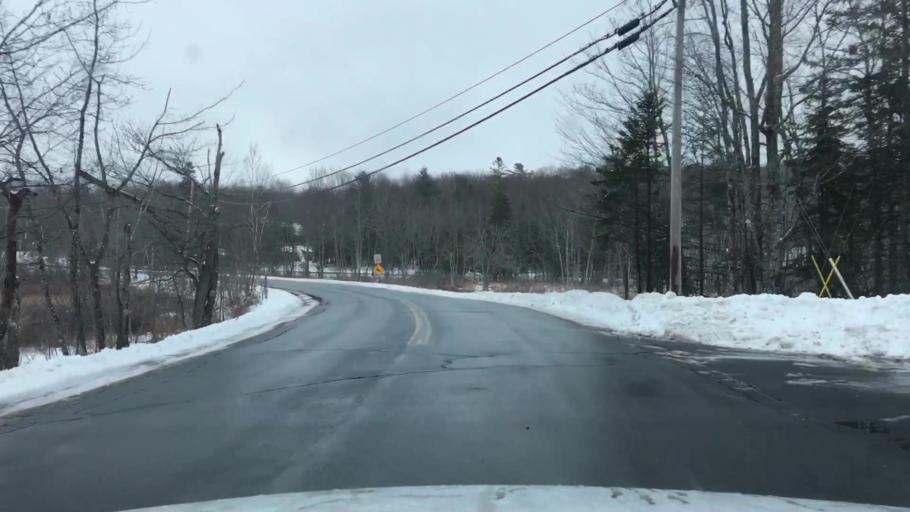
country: US
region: Maine
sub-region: Hancock County
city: Trenton
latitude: 44.4068
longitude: -68.3134
